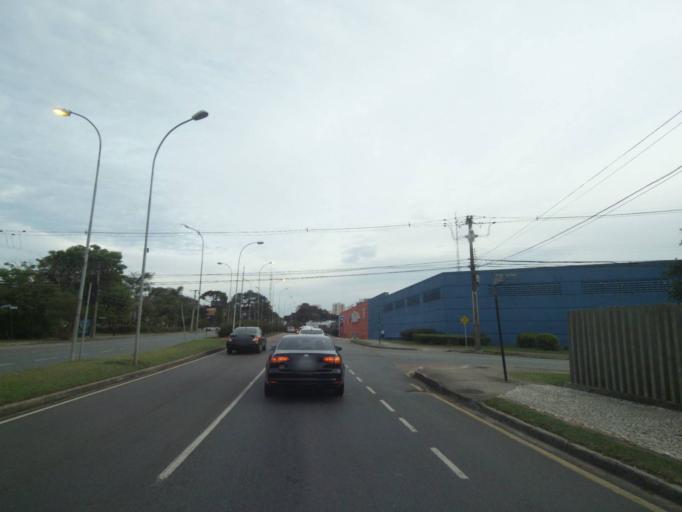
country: BR
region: Parana
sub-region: Curitiba
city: Curitiba
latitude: -25.4291
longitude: -49.2410
